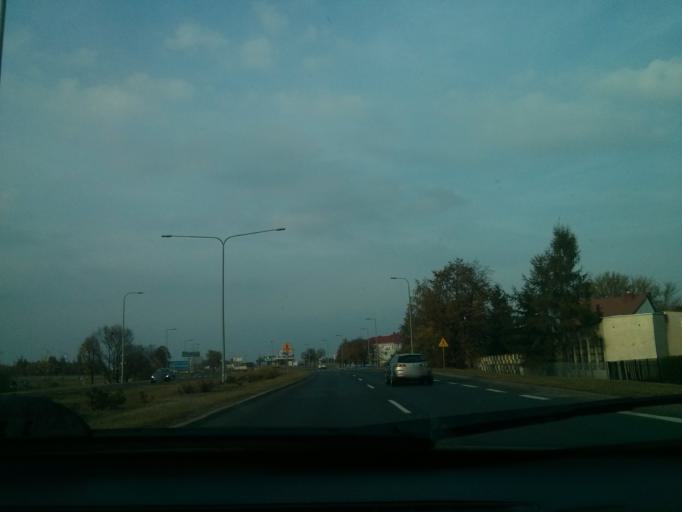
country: PL
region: Masovian Voivodeship
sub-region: Warszawa
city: Kabaty
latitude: 52.1329
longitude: 21.0997
